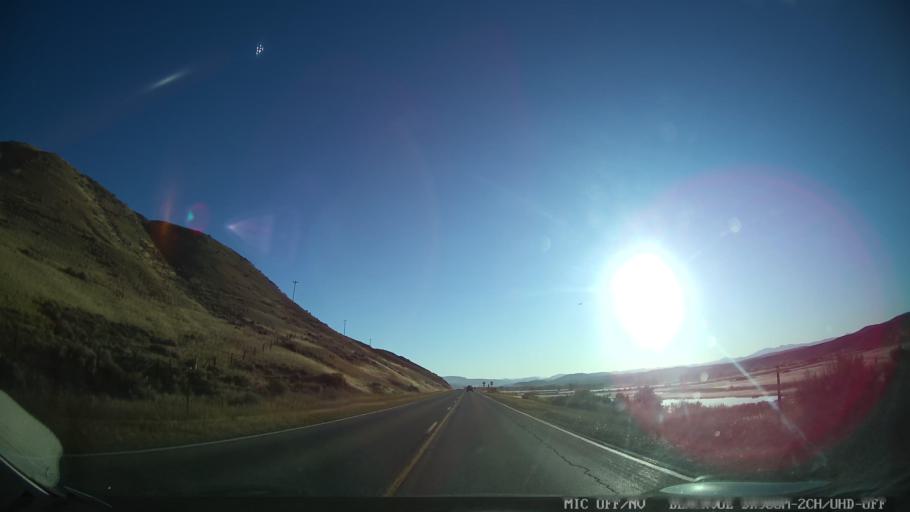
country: US
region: Colorado
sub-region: Grand County
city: Kremmling
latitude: 40.0529
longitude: -106.3405
